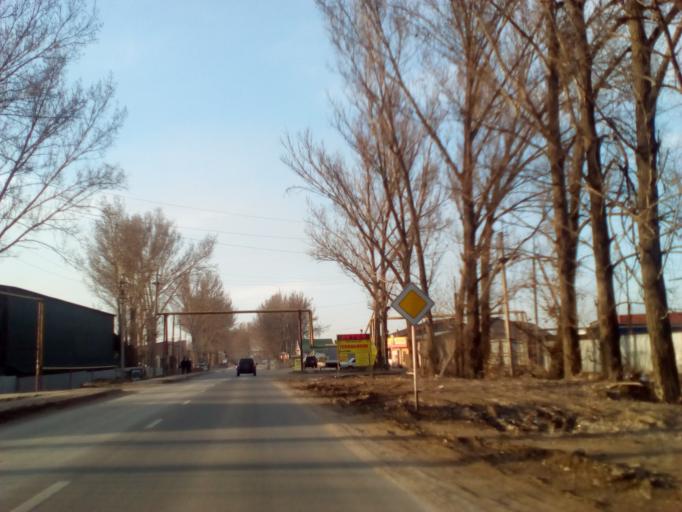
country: KZ
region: Almaty Oblysy
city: Burunday
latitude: 43.2479
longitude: 76.7850
